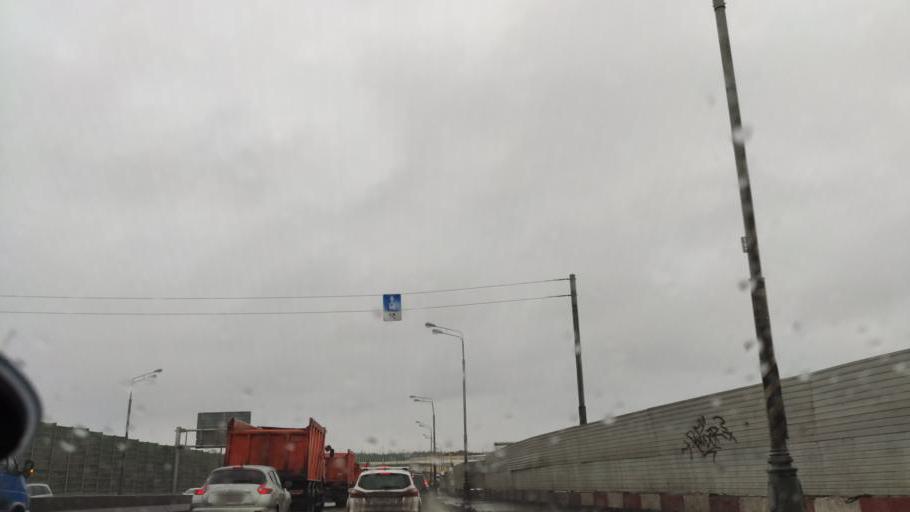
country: RU
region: Moskovskaya
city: Filimonki
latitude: 55.5183
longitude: 37.3734
